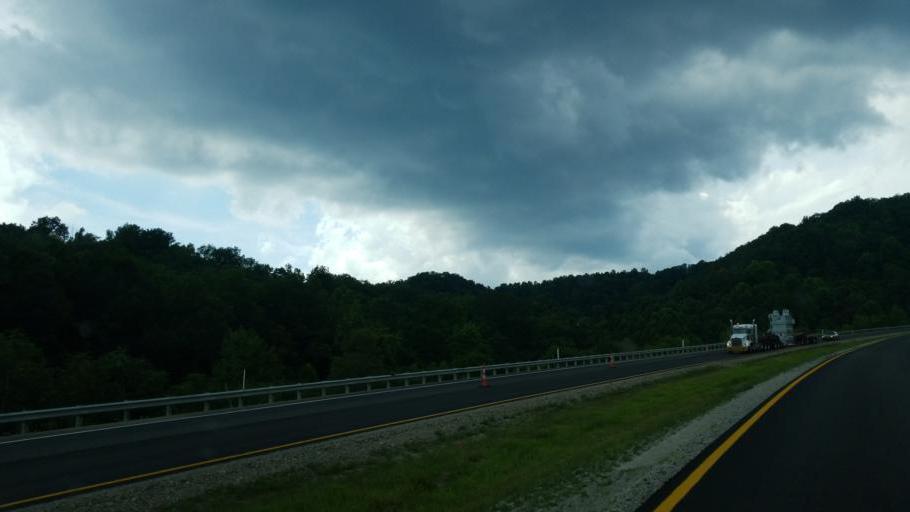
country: US
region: West Virginia
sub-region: Kanawha County
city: Alum Creek
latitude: 38.2650
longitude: -81.8147
